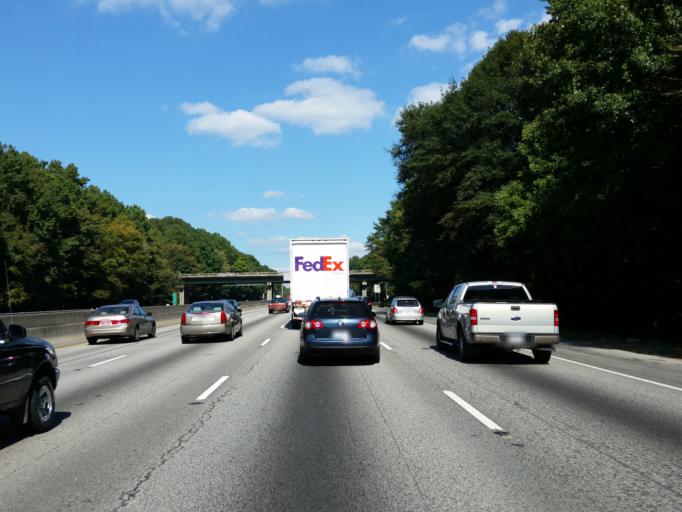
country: US
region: Georgia
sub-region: Clayton County
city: Conley
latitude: 33.6606
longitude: -84.3573
